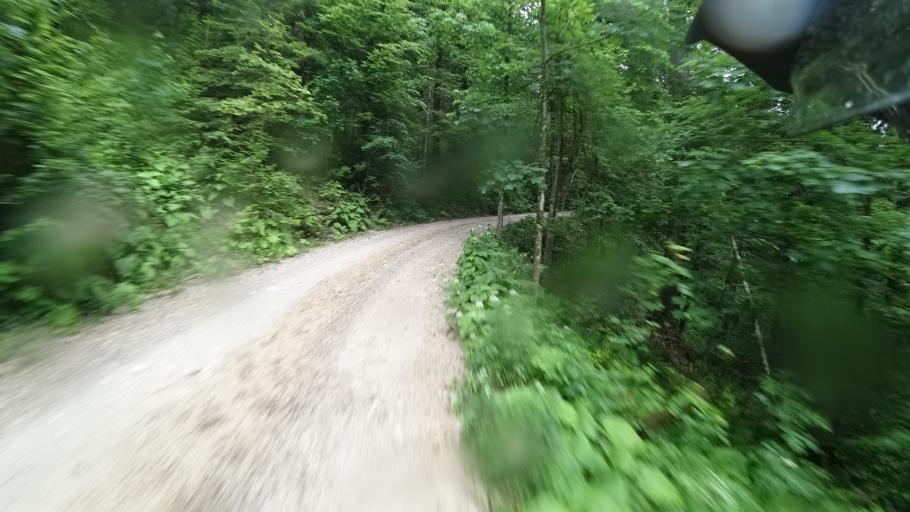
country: HR
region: Primorsko-Goranska
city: Vrbovsko
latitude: 45.3021
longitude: 14.9524
